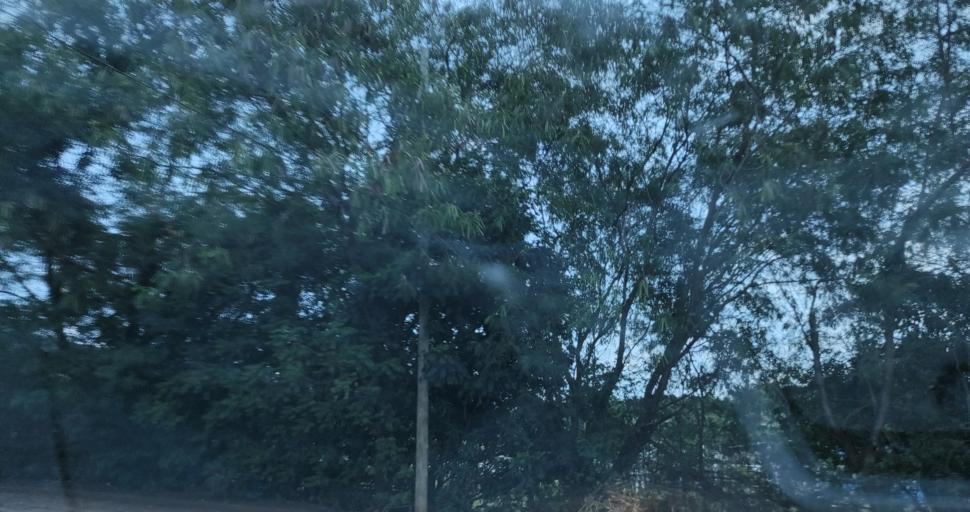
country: AR
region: Misiones
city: Garupa
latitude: -27.4718
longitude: -55.8478
